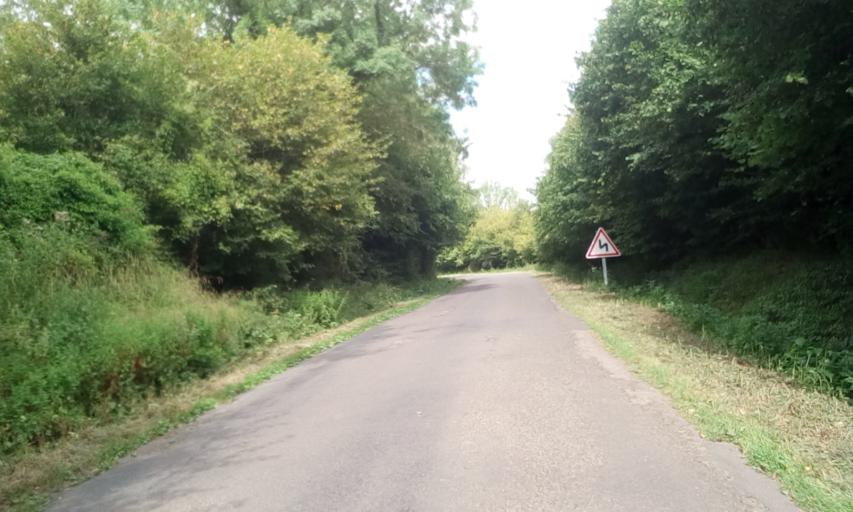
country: FR
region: Lower Normandy
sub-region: Departement du Calvados
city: Sannerville
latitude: 49.1723
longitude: -0.2067
